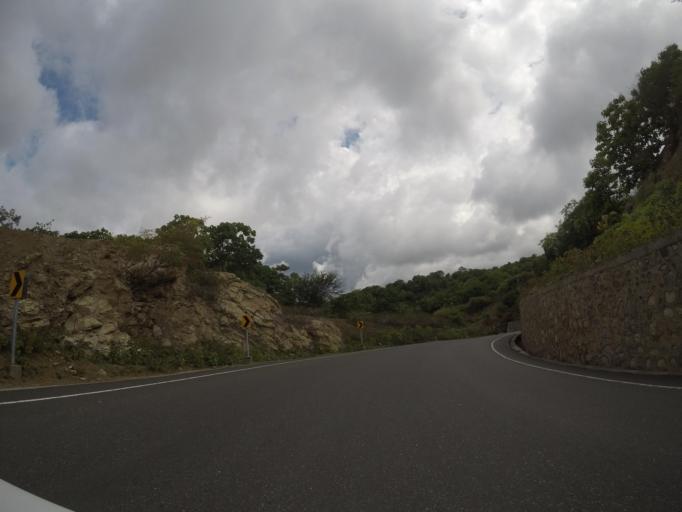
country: TL
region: Liquica
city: Maubara
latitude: -8.7440
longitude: 125.1283
